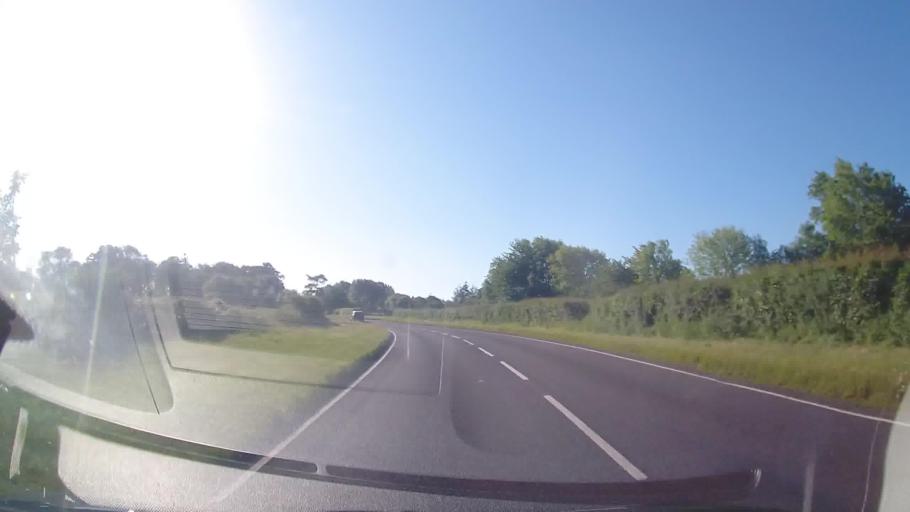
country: GB
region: England
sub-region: Telford and Wrekin
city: Eyton upon the Weald Moors
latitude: 52.7229
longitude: -2.5435
